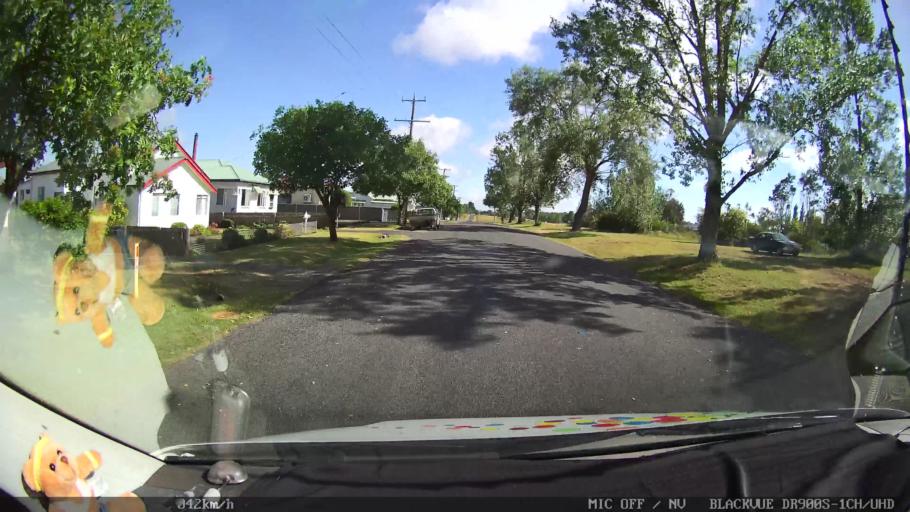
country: AU
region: New South Wales
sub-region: Guyra
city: Guyra
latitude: -30.2133
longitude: 151.6730
